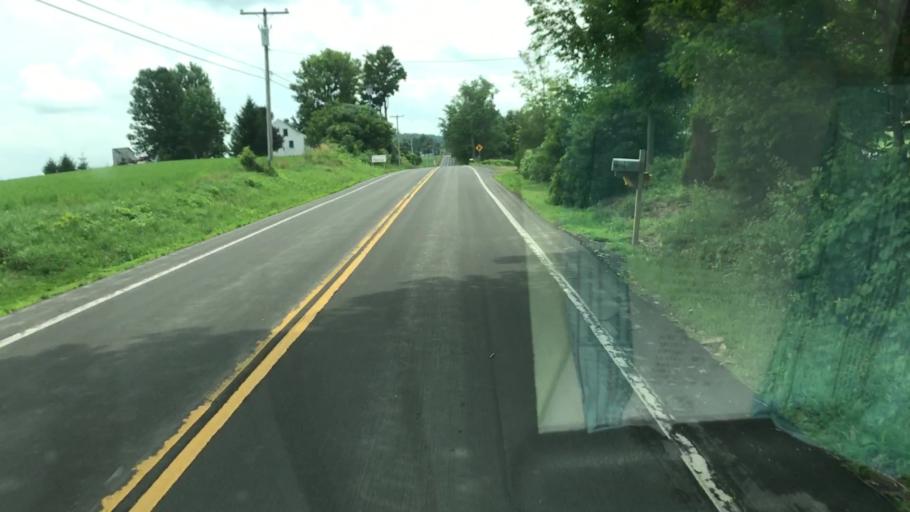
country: US
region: New York
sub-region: Onondaga County
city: Manlius
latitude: 42.9311
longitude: -75.9766
